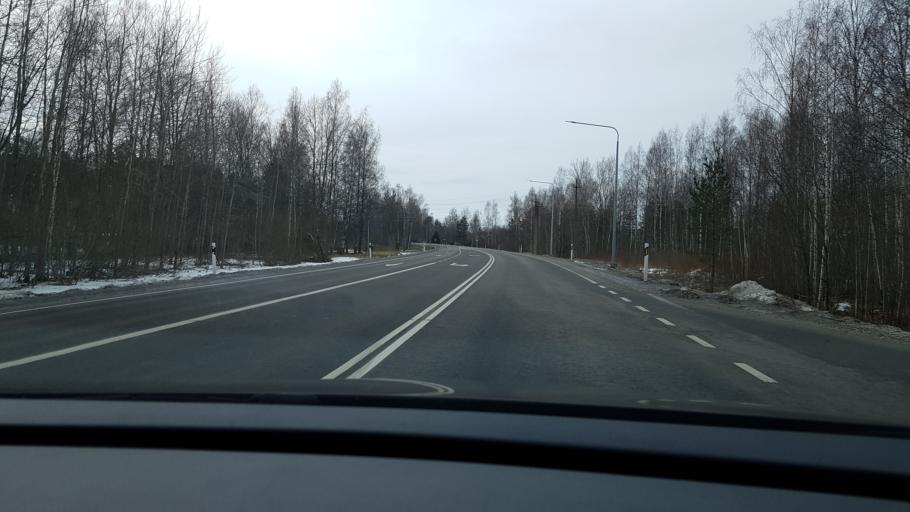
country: EE
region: Paernumaa
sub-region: Sindi linn
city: Sindi
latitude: 58.4104
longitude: 24.6735
